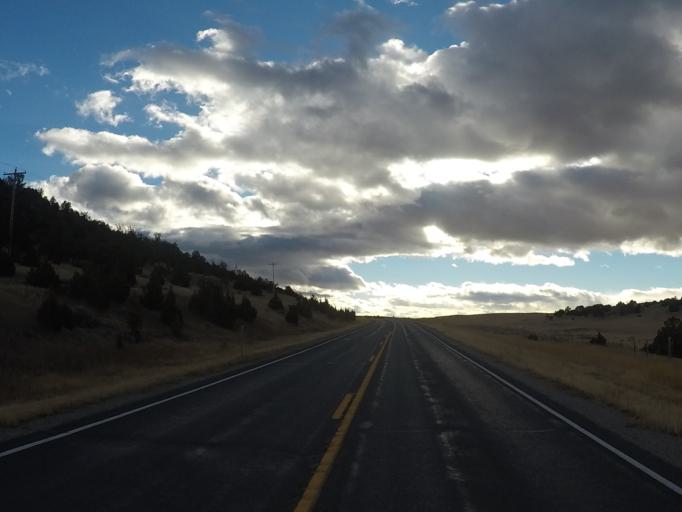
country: US
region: Montana
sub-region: Jefferson County
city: Whitehall
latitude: 45.9008
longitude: -111.9545
